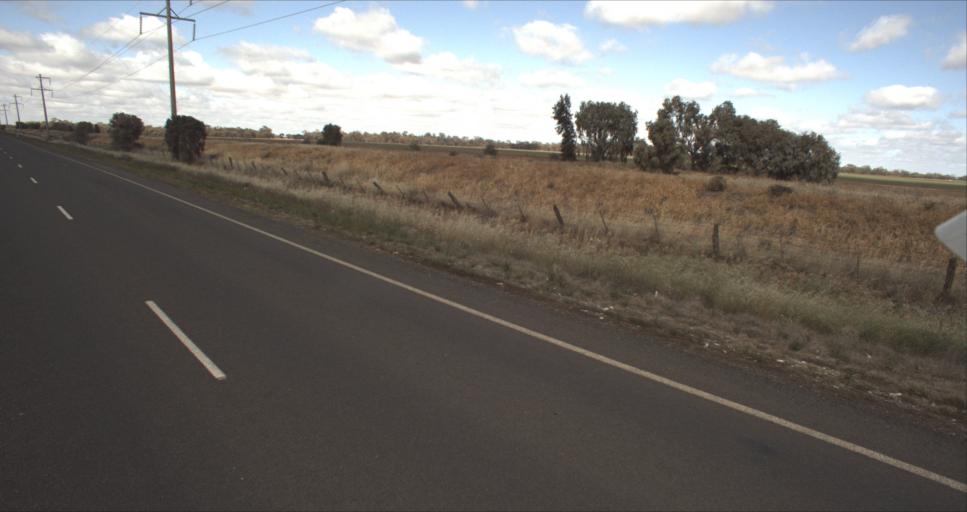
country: AU
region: New South Wales
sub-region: Murrumbidgee Shire
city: Darlington Point
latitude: -34.5348
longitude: 146.1732
